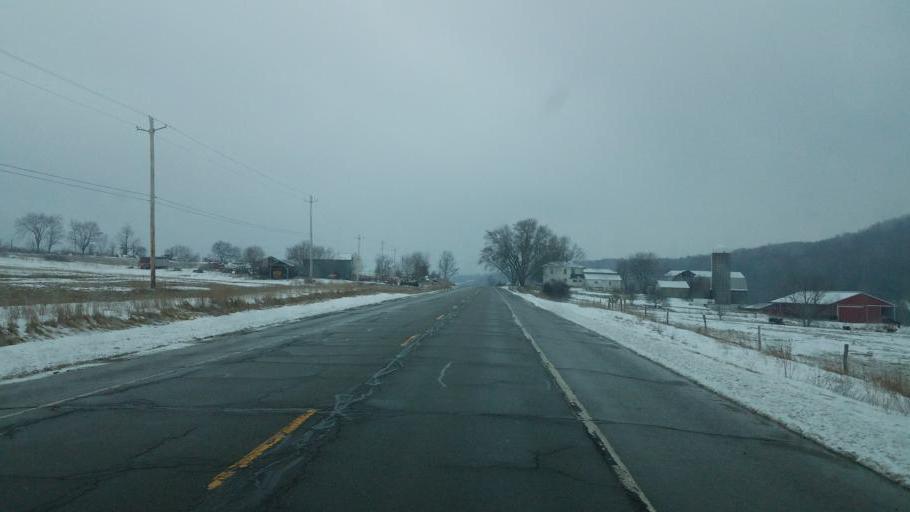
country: US
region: Pennsylvania
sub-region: Tioga County
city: Elkland
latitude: 42.0999
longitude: -77.4468
